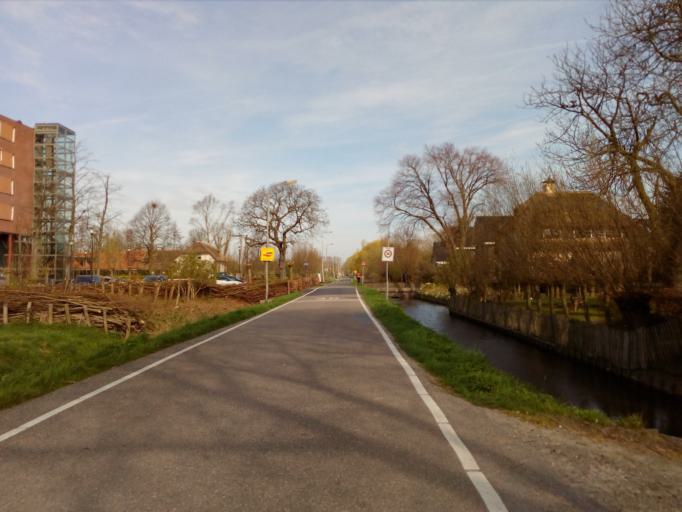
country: NL
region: South Holland
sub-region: Gemeente Delft
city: Delft
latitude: 51.9790
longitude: 4.3559
